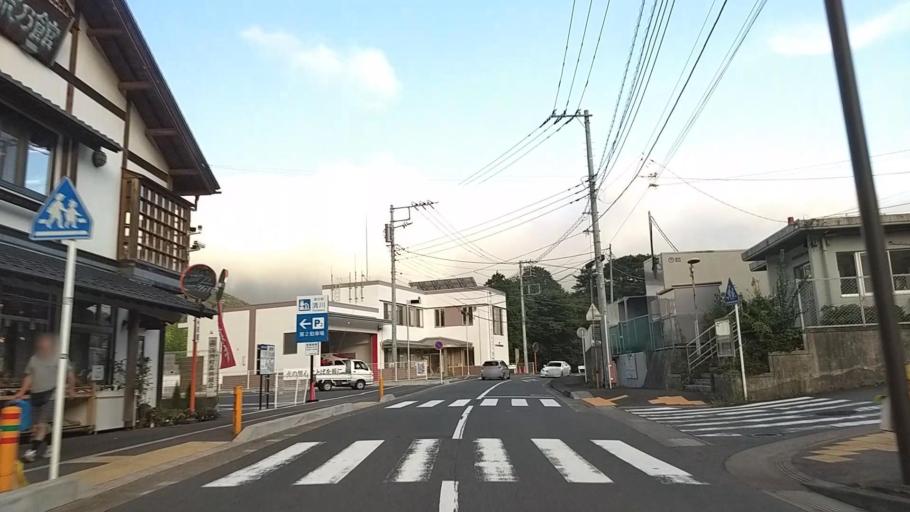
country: JP
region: Kanagawa
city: Atsugi
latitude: 35.4825
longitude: 139.2770
